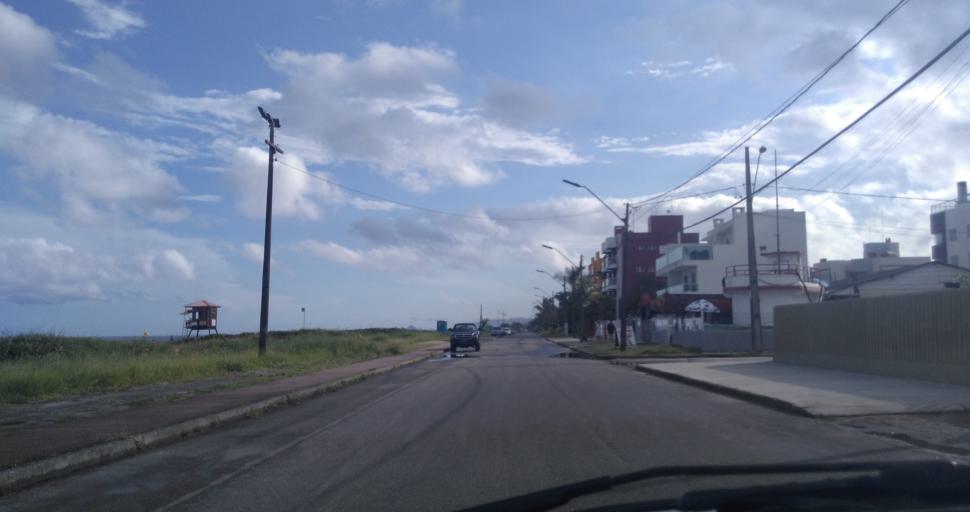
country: BR
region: Parana
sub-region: Pontal Do Parana
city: Pontal do Parana
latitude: -25.7319
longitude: -48.4896
